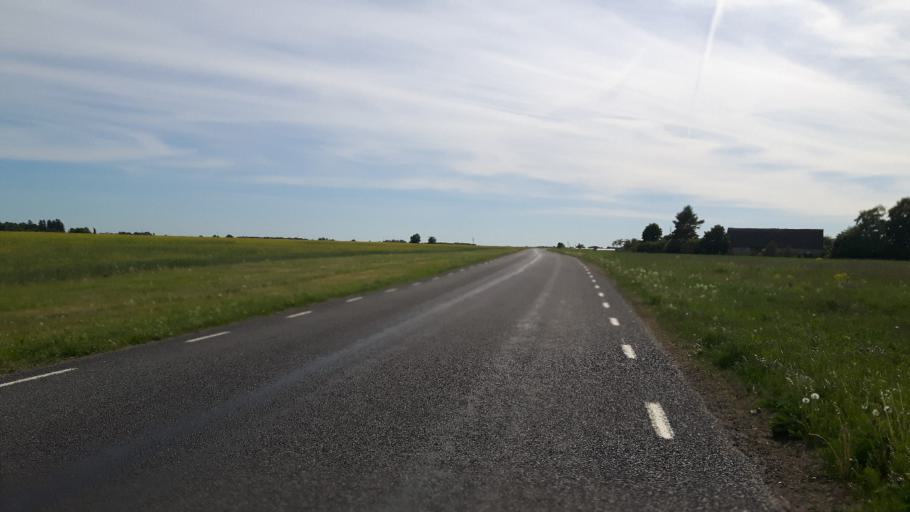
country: EE
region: Harju
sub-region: Raasiku vald
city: Arukula
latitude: 59.4381
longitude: 25.1284
